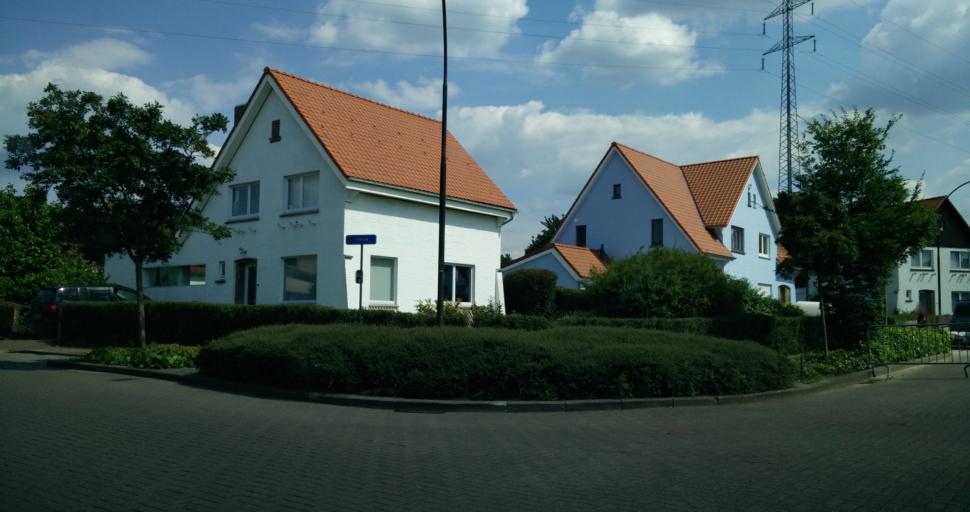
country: BE
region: Flanders
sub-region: Provincie Vlaams-Brabant
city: Halle
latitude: 50.7372
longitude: 4.2520
